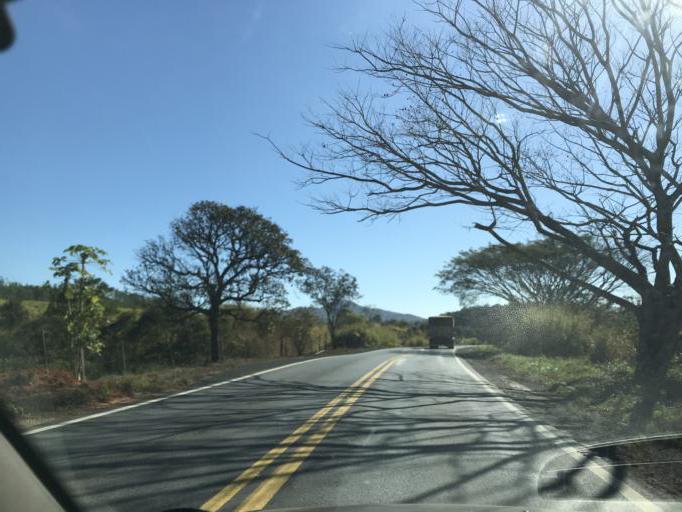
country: BR
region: Minas Gerais
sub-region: Bambui
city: Bambui
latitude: -19.8547
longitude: -45.9917
